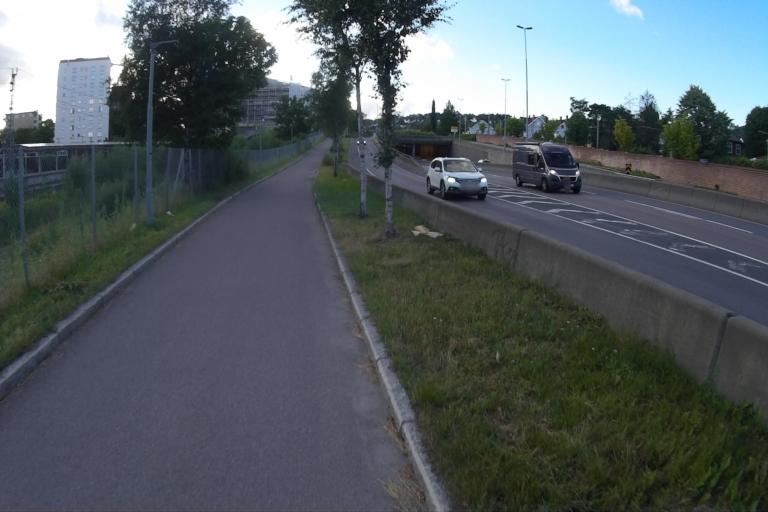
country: NO
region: Oslo
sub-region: Oslo
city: Oslo
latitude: 59.9436
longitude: 10.7798
